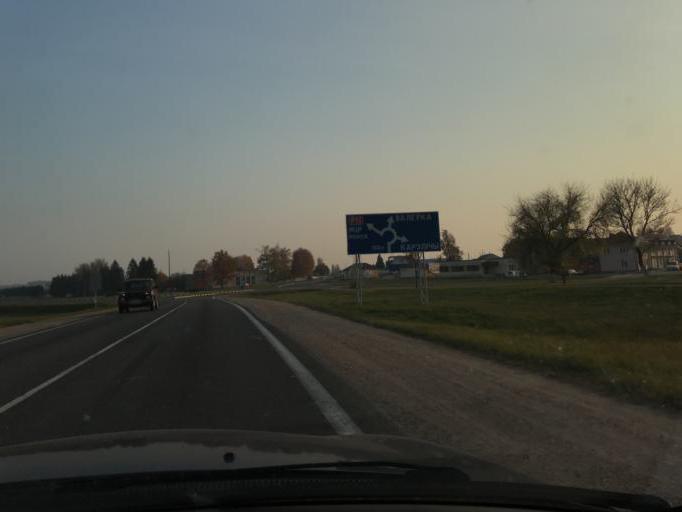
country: BY
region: Grodnenskaya
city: Karelichy
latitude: 53.5596
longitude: 26.1520
